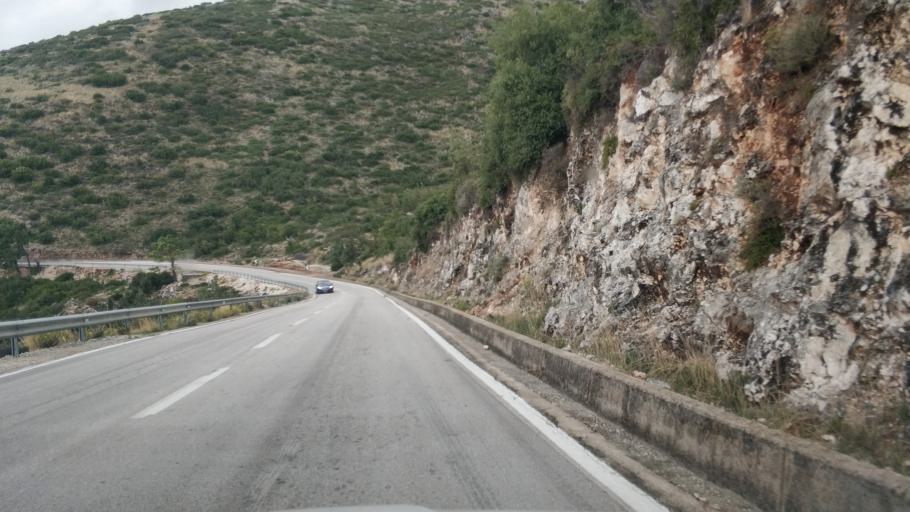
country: AL
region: Vlore
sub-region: Rrethi i Vlores
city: Vranisht
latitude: 40.1446
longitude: 19.6610
